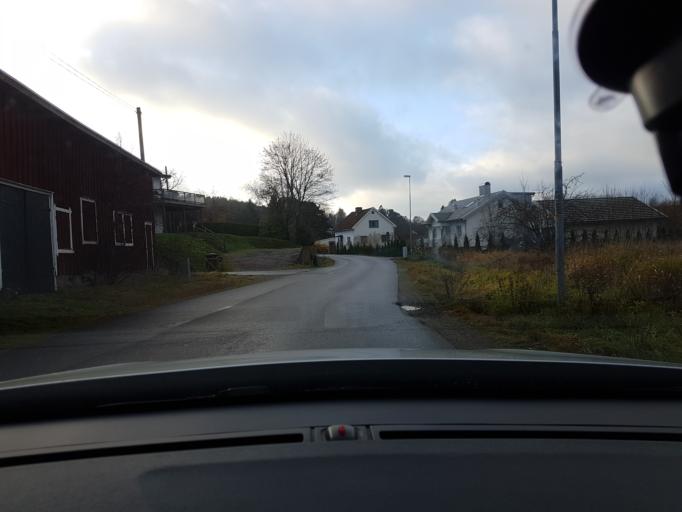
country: SE
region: Vaestra Goetaland
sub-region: Ale Kommun
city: Alafors
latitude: 57.9213
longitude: 12.0737
